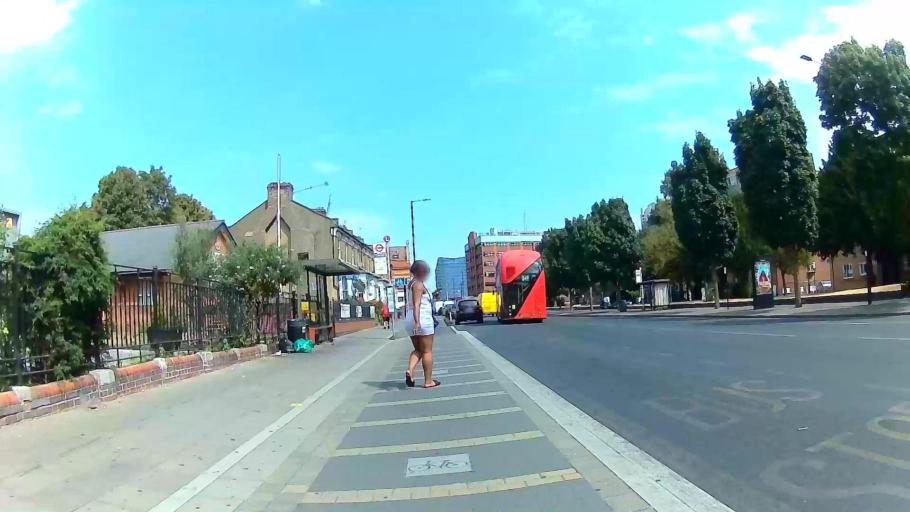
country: GB
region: England
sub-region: Greater London
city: Enfield
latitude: 51.6207
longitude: -0.0621
